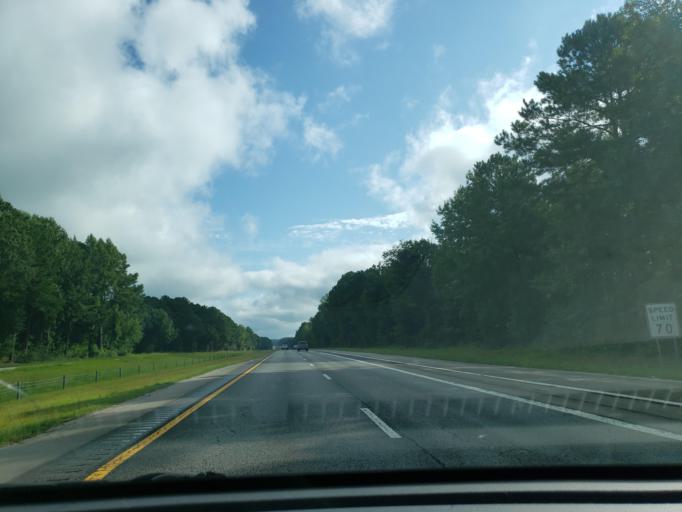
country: US
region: North Carolina
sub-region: Wake County
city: Zebulon
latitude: 35.8367
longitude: -78.3015
